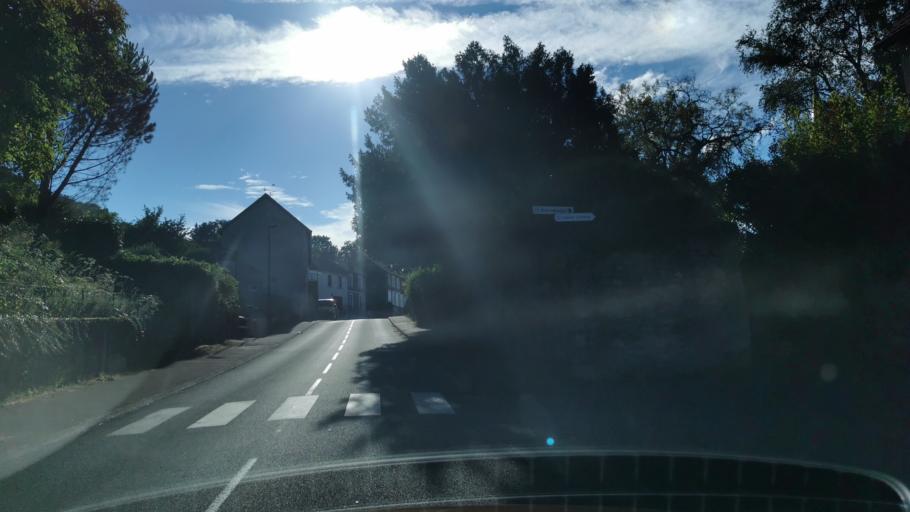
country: FR
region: Bourgogne
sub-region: Departement de Saone-et-Loire
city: Marmagne
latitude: 46.8393
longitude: 4.3325
